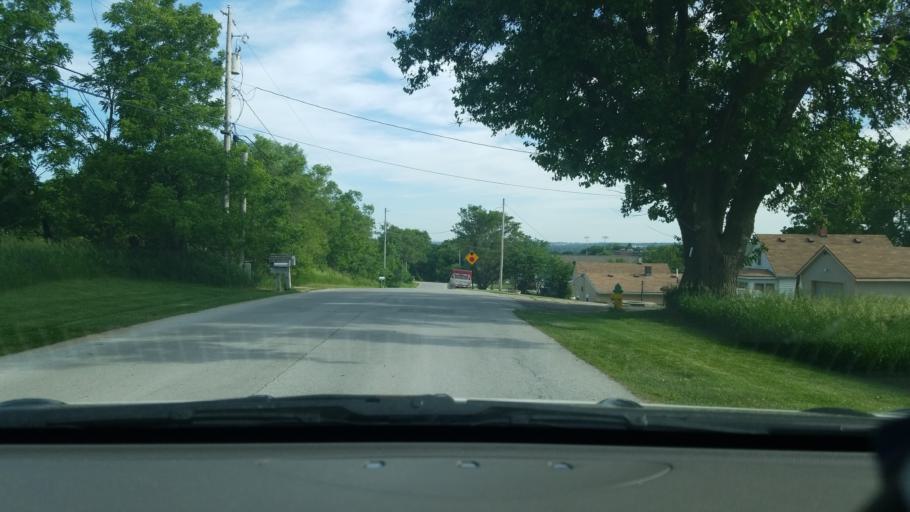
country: US
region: Nebraska
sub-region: Sarpy County
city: Offutt Air Force Base
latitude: 41.1693
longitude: -95.9335
